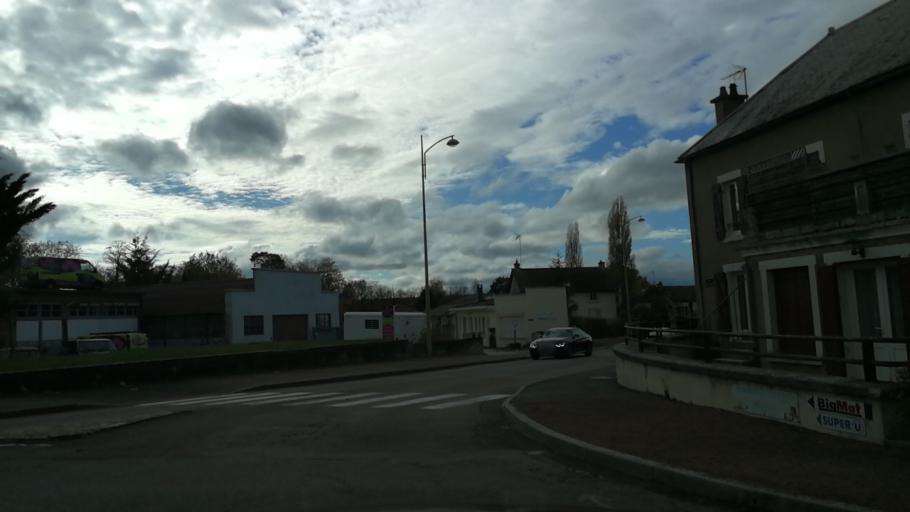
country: FR
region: Bourgogne
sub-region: Departement de la Cote-d'Or
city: Pouilly-en-Auxois
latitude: 47.2691
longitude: 4.5466
